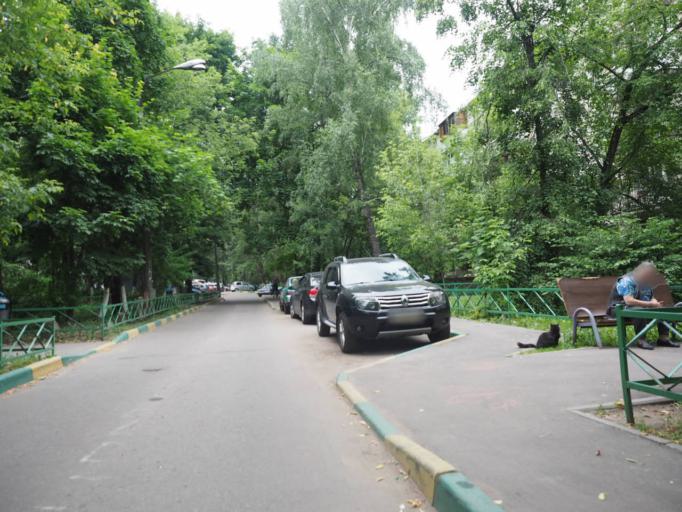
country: RU
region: Moskovskaya
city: Lyubertsy
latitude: 55.6589
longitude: 37.9023
